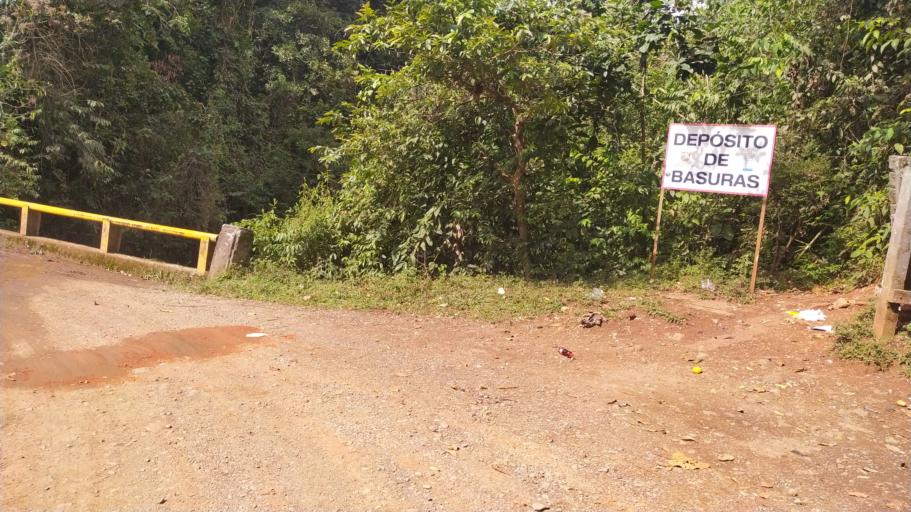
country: CO
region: Valle del Cauca
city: Cali
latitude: 3.4347
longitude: -76.6142
